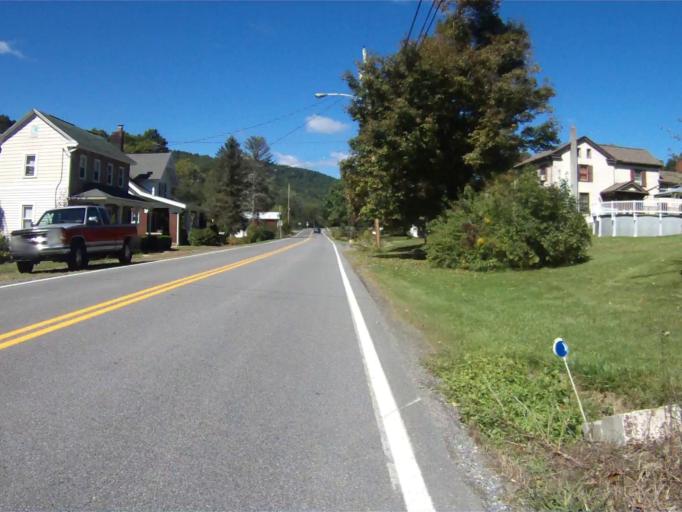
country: US
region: Pennsylvania
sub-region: Centre County
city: Houserville
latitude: 40.9082
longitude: -77.8791
